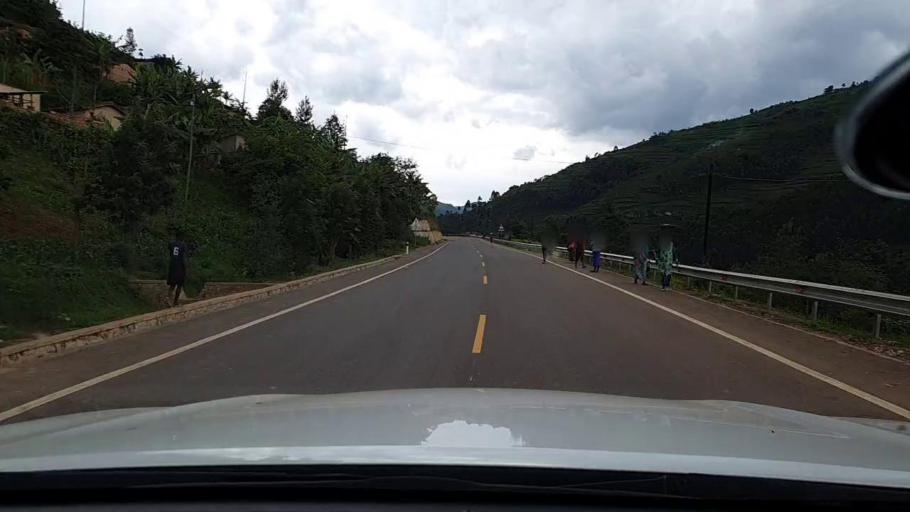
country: RW
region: Northern Province
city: Byumba
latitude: -1.6457
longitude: 29.9239
